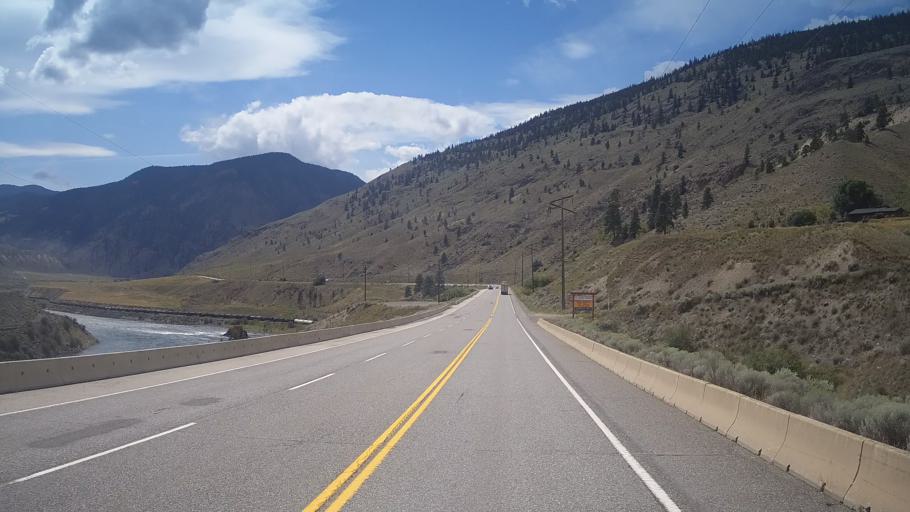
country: CA
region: British Columbia
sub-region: Thompson-Nicola Regional District
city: Ashcroft
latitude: 50.4540
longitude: -121.3076
